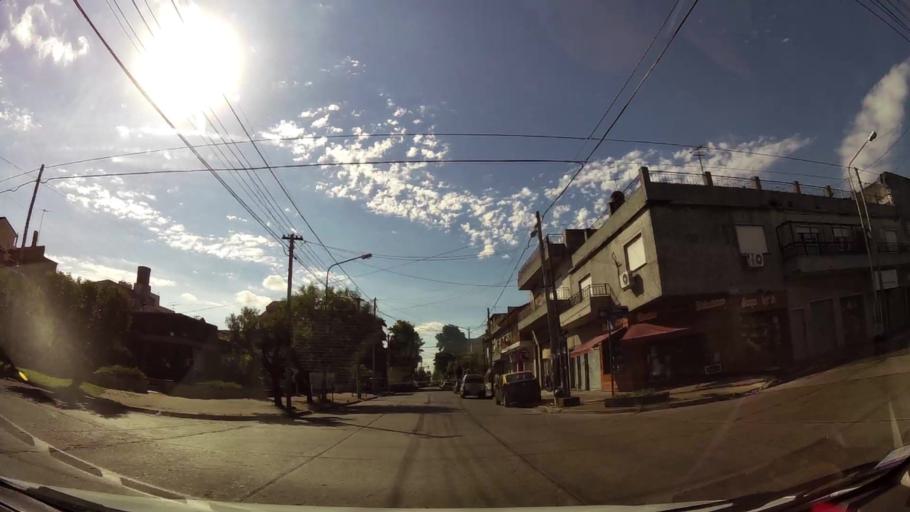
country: AR
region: Buenos Aires
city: San Justo
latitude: -34.6612
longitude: -58.5837
